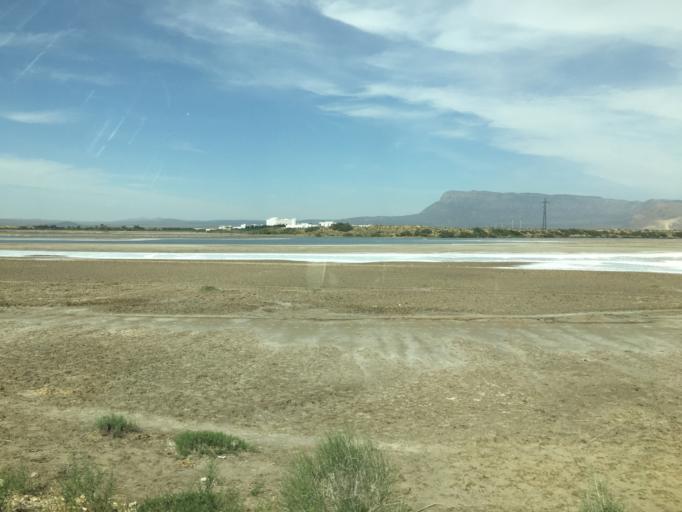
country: TM
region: Balkan
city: Balkanabat
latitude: 39.6186
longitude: 54.1633
